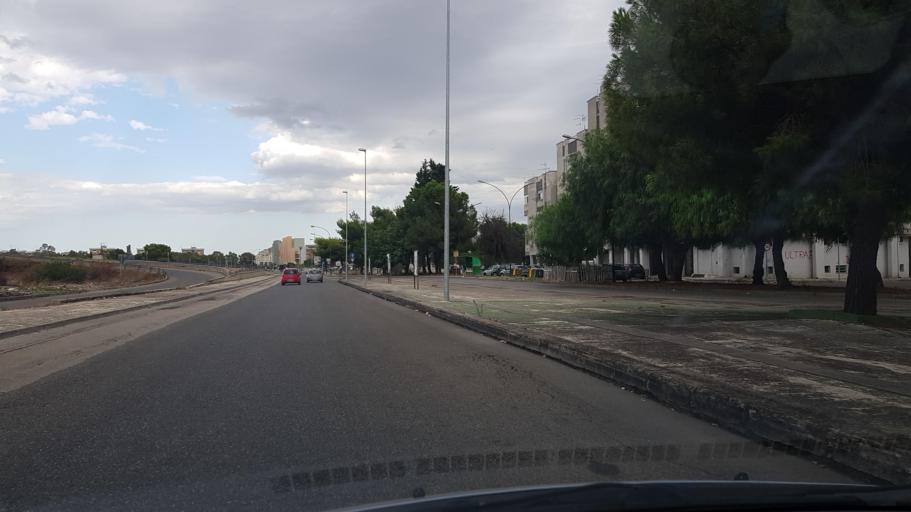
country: IT
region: Apulia
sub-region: Provincia di Taranto
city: Paolo VI
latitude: 40.5201
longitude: 17.2606
